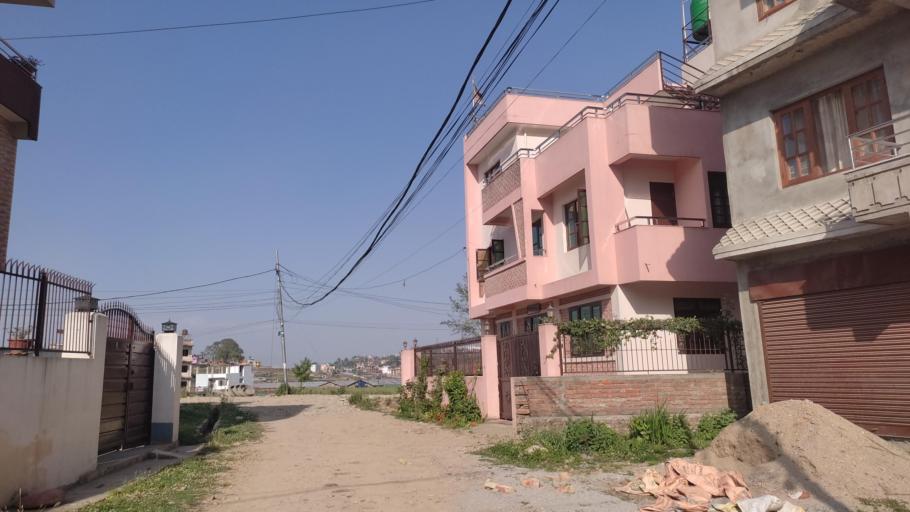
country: NP
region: Central Region
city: Kirtipur
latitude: 27.6600
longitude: 85.2668
